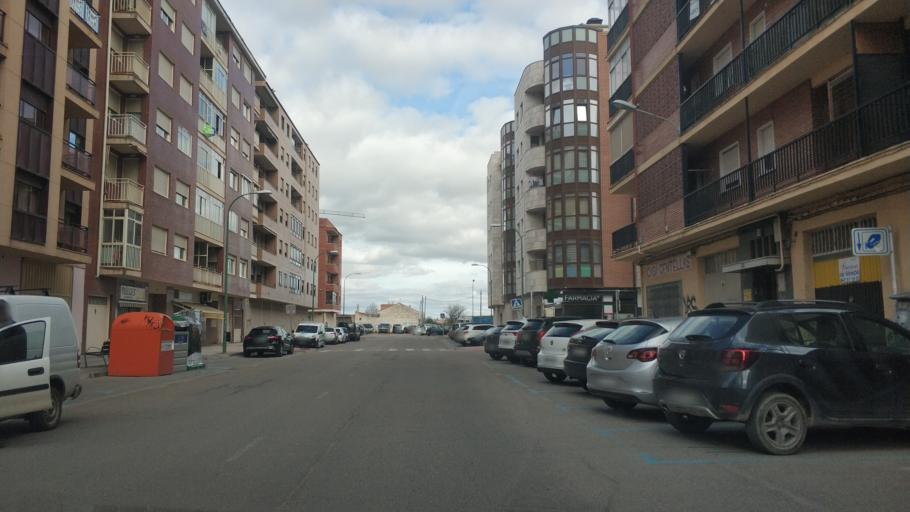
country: ES
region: Castille and Leon
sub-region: Provincia de Burgos
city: Aranda de Duero
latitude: 41.6737
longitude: -3.6834
